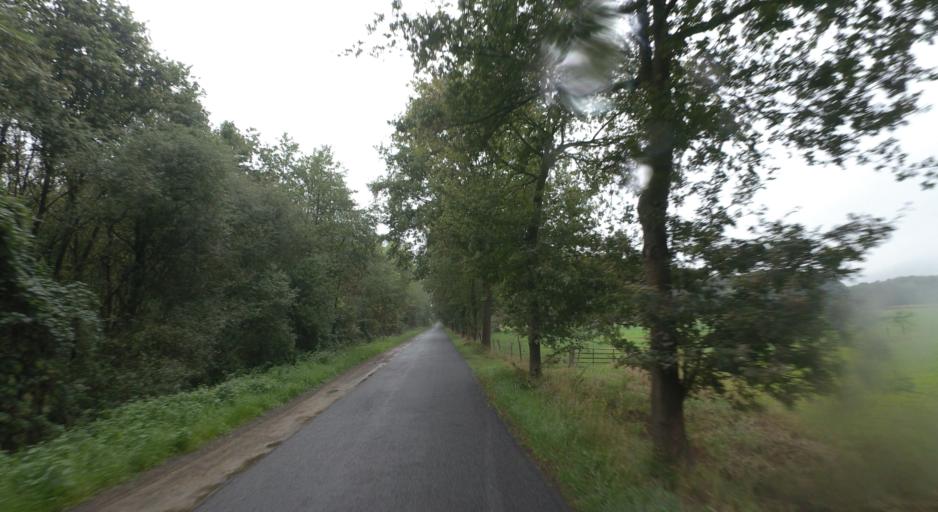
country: DE
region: North Rhine-Westphalia
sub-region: Regierungsbezirk Dusseldorf
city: Hamminkeln
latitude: 51.7135
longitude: 6.6136
